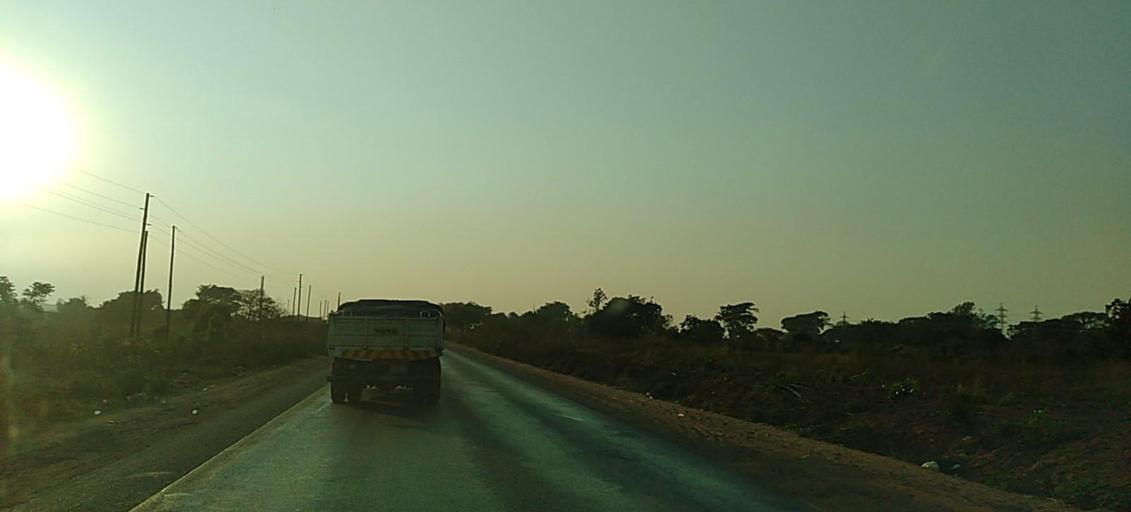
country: ZM
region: Copperbelt
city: Ndola
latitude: -13.0225
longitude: 28.6725
